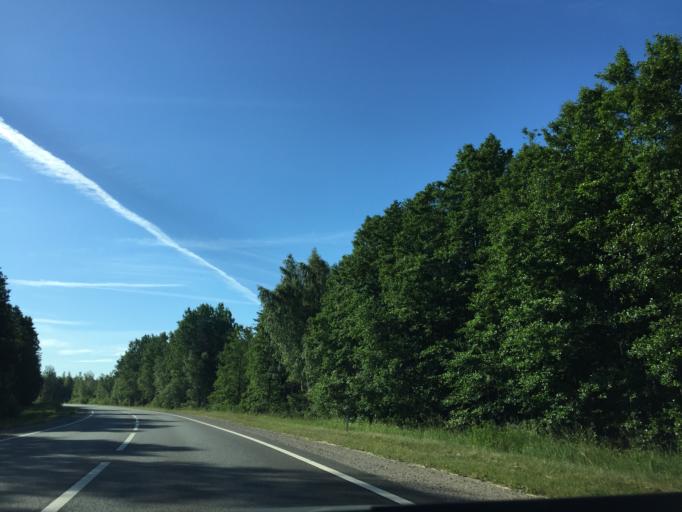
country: LV
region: Ventspils
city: Ventspils
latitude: 57.3797
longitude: 21.7144
